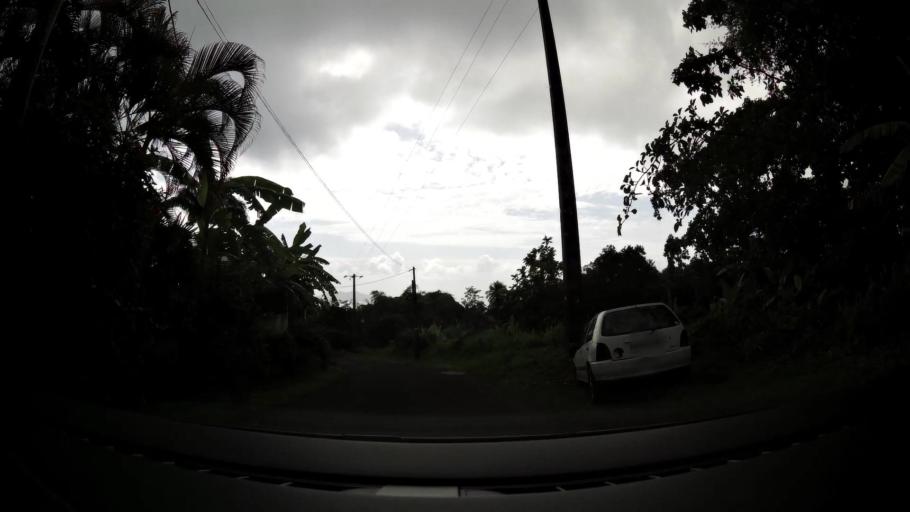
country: GP
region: Guadeloupe
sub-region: Guadeloupe
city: Trois-Rivieres
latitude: 15.9831
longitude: -61.6372
